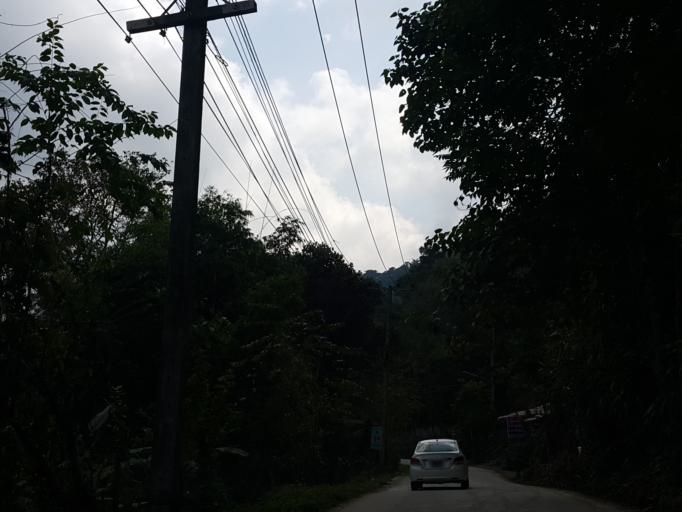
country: TH
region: Chiang Mai
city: Mae On
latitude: 18.8684
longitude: 99.3197
